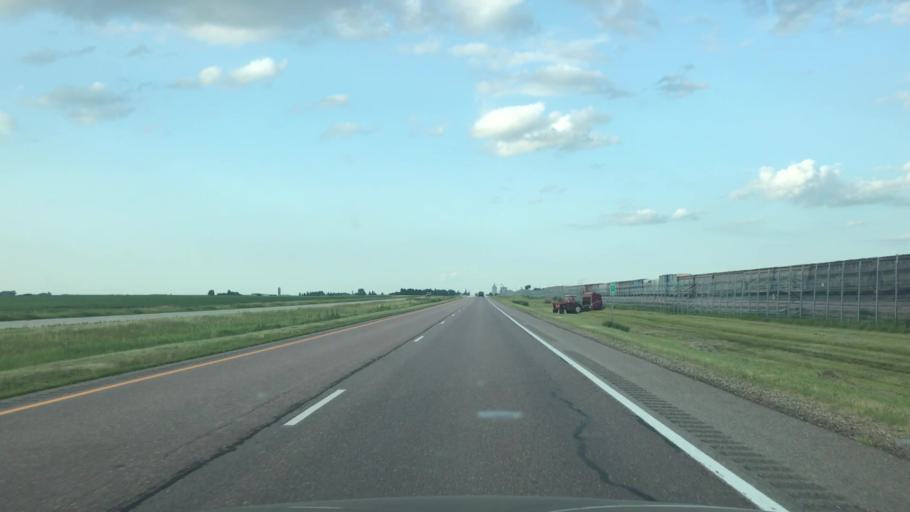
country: US
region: Minnesota
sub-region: Nobles County
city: Worthington
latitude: 43.6728
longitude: -95.5111
